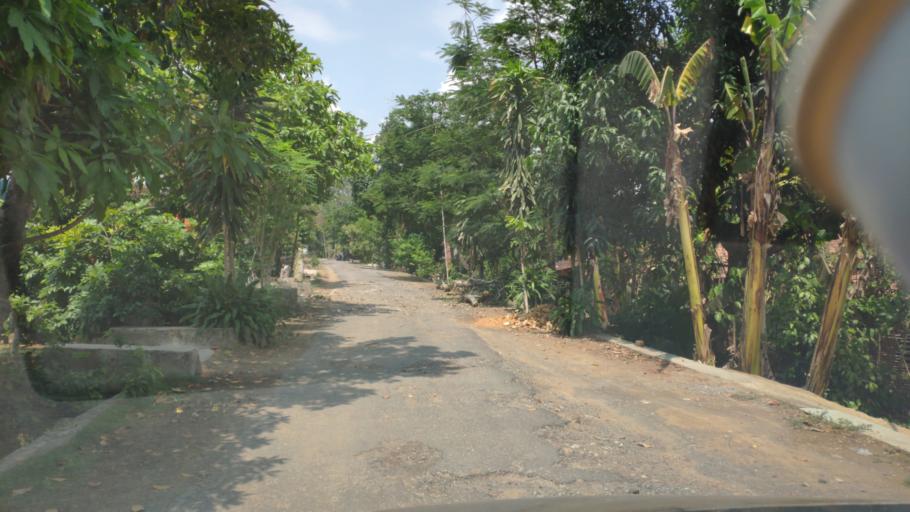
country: ID
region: Central Java
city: Jepang
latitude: -7.0084
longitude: 111.2330
